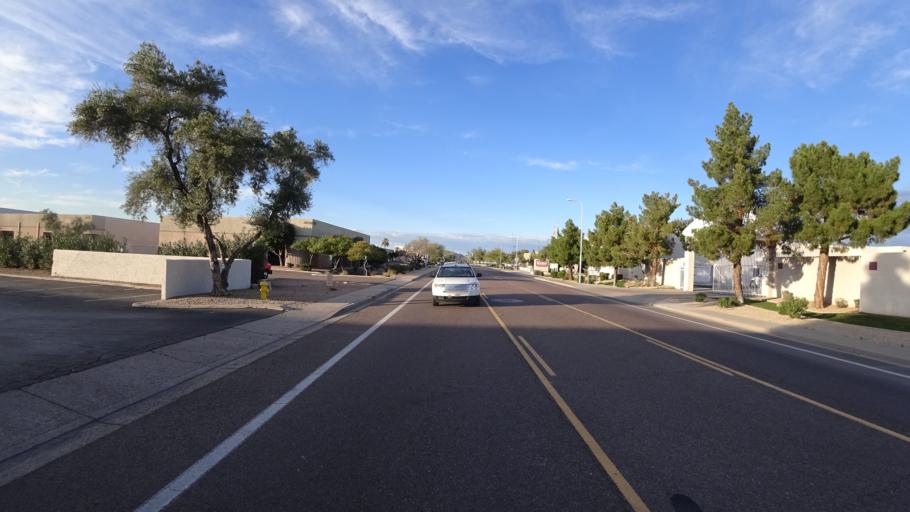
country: US
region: Arizona
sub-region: Maricopa County
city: Tempe Junction
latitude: 33.3981
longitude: -111.9522
